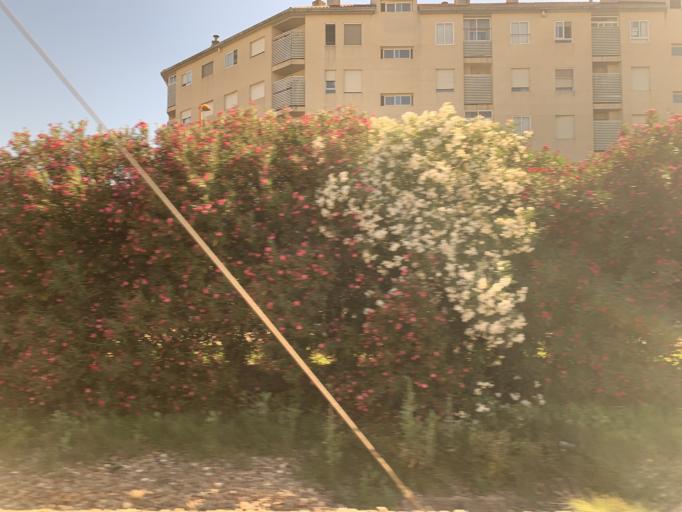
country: ES
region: Aragon
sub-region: Provincia de Zaragoza
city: Utebo
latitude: 41.7097
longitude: -0.9964
